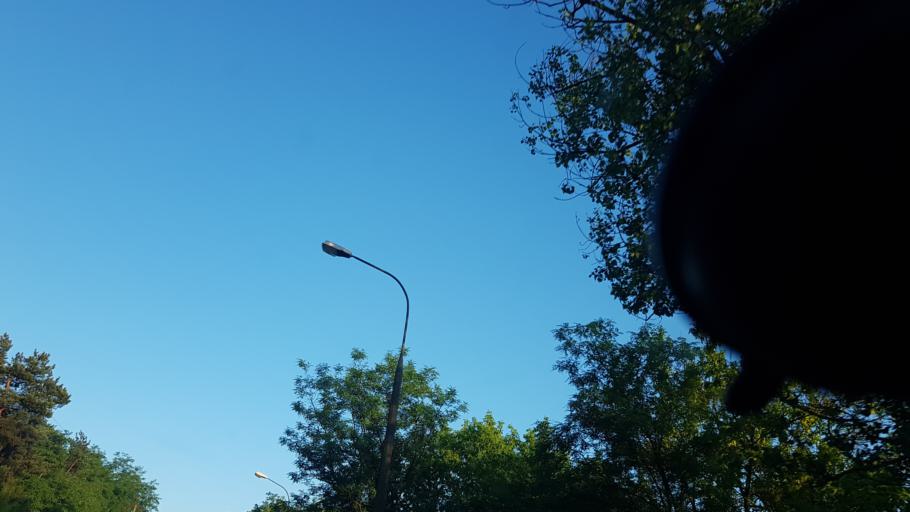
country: PL
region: Masovian Voivodeship
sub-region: Warszawa
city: Wawer
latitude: 52.1675
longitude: 21.2057
